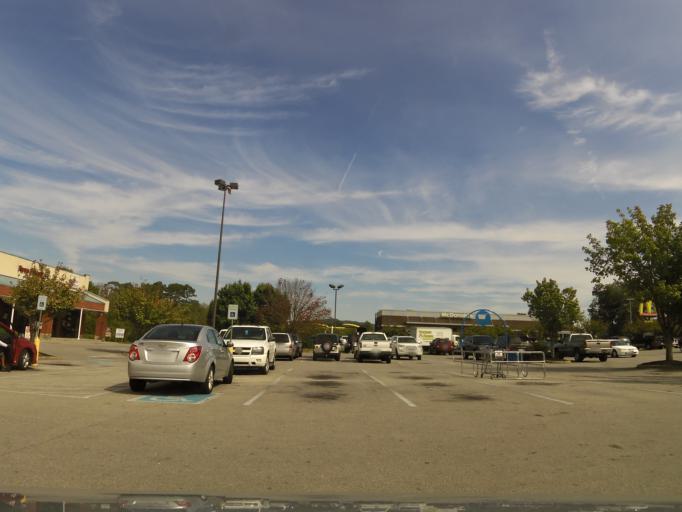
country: US
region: Tennessee
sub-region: Blount County
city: Eagleton Village
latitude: 35.8015
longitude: -83.9442
